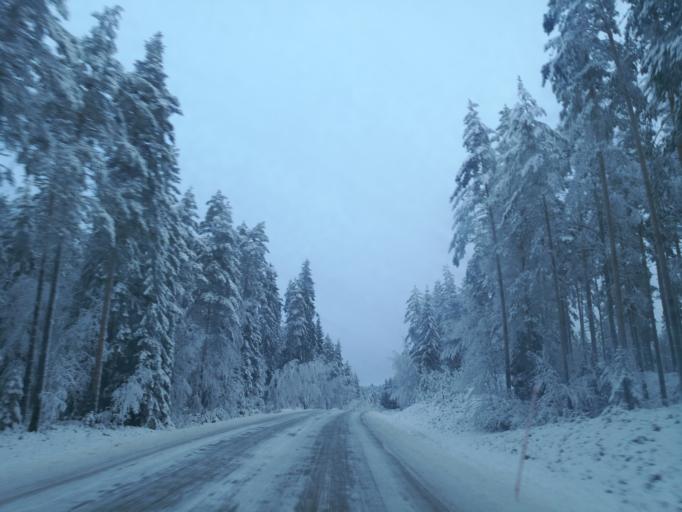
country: NO
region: Hedmark
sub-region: Grue
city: Kirkenaer
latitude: 60.3853
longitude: 12.3597
